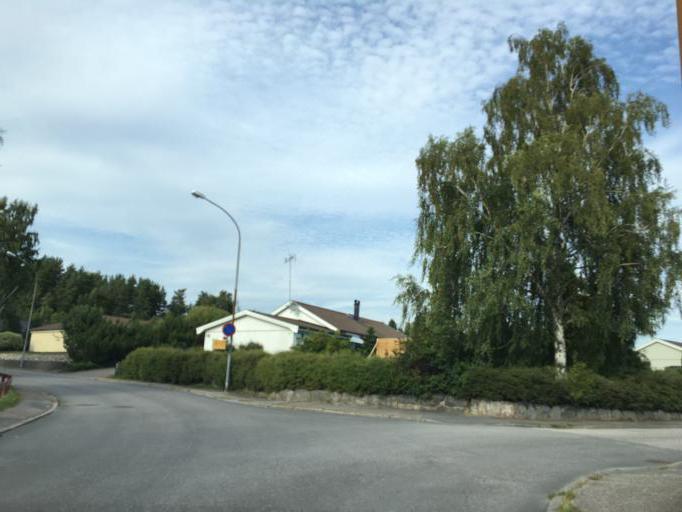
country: SE
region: Soedermanland
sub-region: Eskilstuna Kommun
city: Eskilstuna
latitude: 59.3938
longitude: 16.4997
